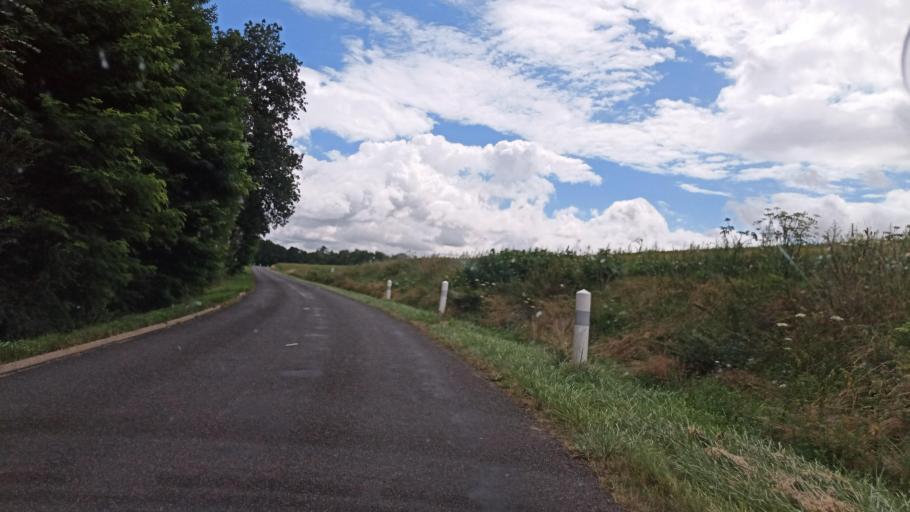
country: FR
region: Ile-de-France
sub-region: Departement de Seine-et-Marne
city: Voulx
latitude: 48.2610
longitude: 3.0125
